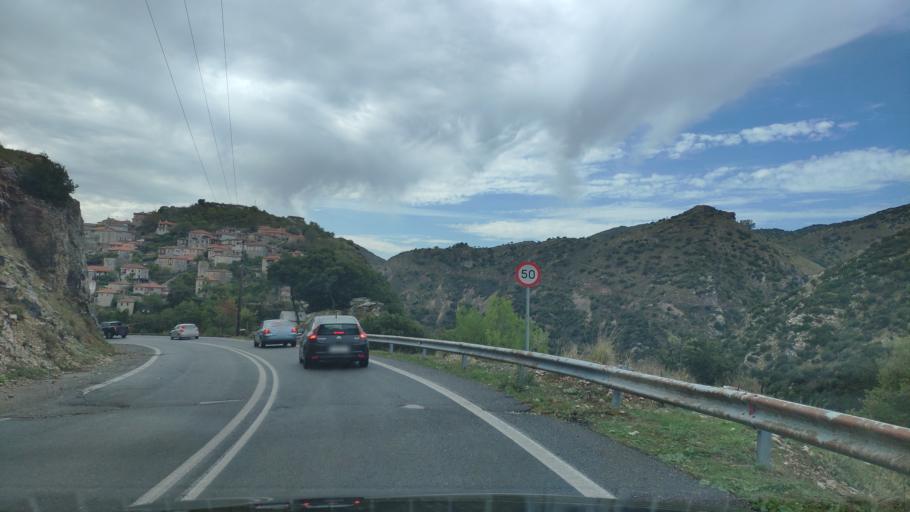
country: GR
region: Peloponnese
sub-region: Nomos Arkadias
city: Dimitsana
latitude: 37.6013
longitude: 22.0390
